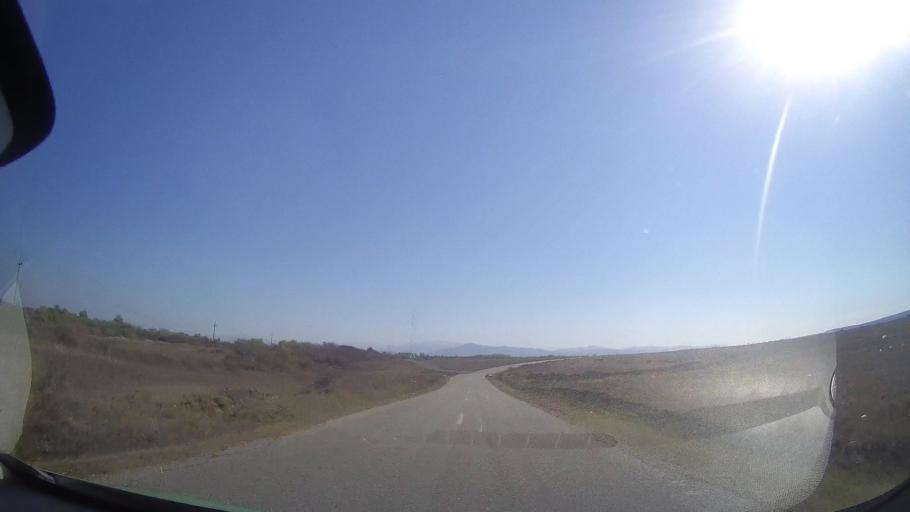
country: RO
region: Timis
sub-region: Comuna Traian Vuia
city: Traian Vuia
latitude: 45.8013
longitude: 22.0072
